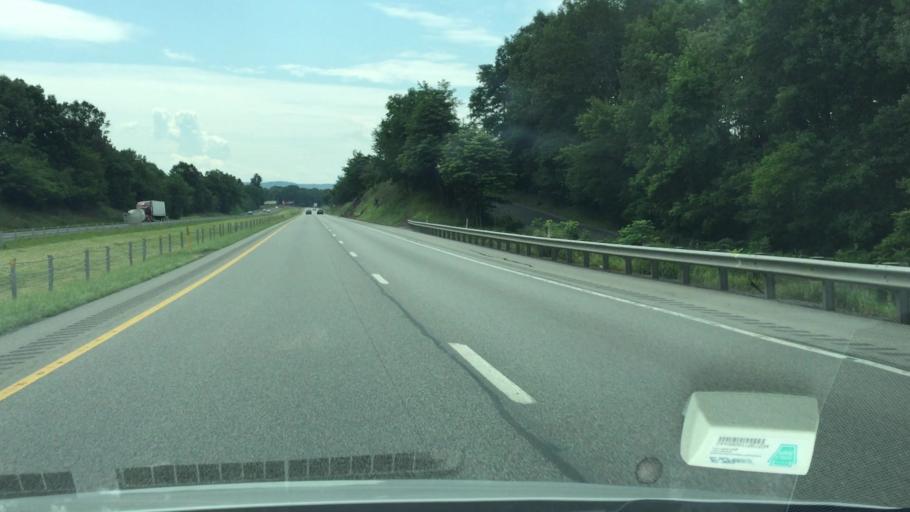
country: US
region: Maryland
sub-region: Washington County
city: Hancock
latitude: 39.8268
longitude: -78.2737
